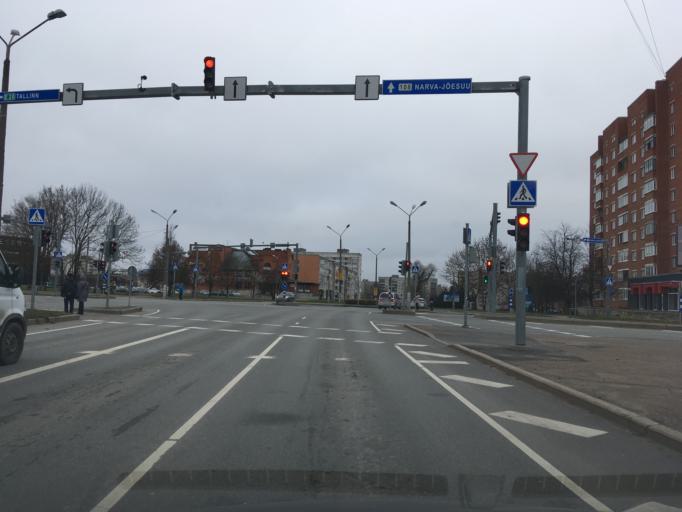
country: EE
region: Ida-Virumaa
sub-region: Narva linn
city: Narva
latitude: 59.3793
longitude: 28.1795
